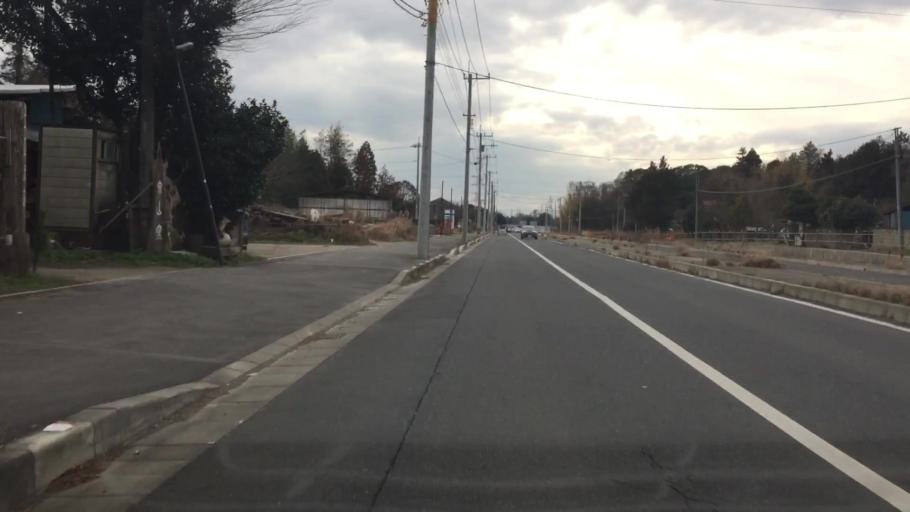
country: JP
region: Chiba
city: Shiroi
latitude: 35.7976
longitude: 140.0926
